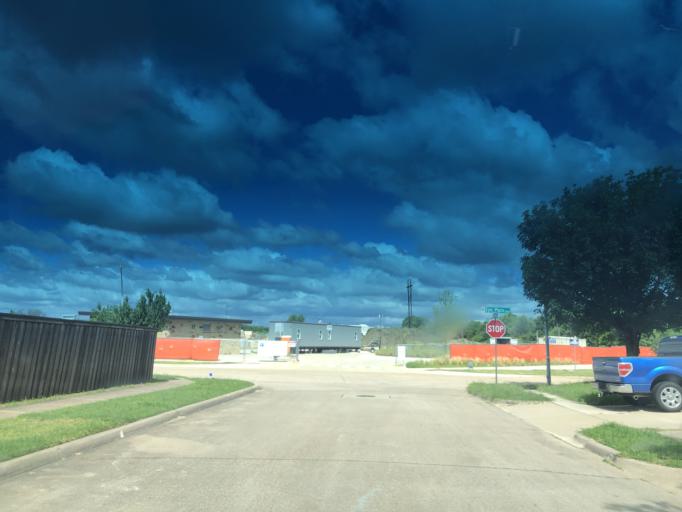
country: US
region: Texas
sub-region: Dallas County
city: Grand Prairie
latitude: 32.6999
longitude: -97.0325
